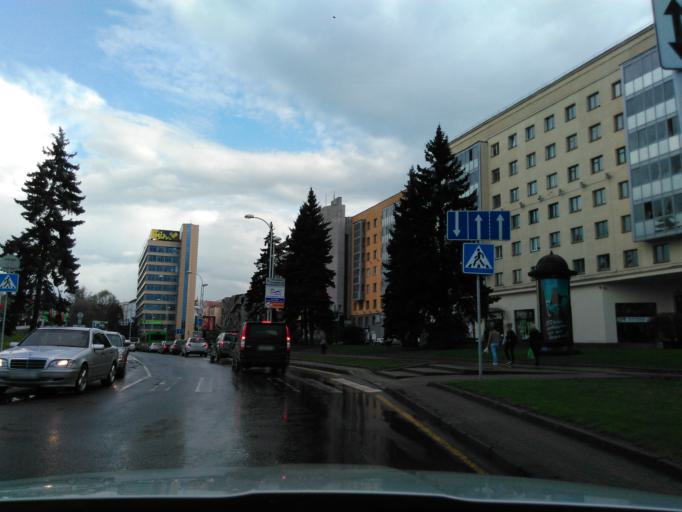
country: BY
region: Minsk
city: Minsk
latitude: 53.9066
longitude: 27.5516
